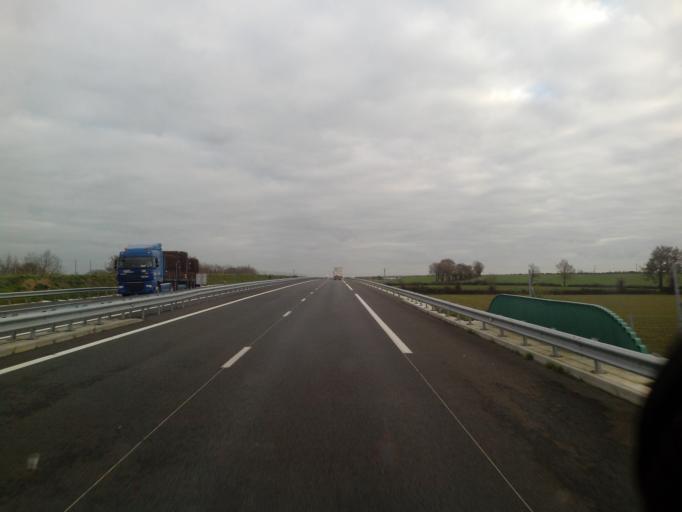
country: FR
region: Poitou-Charentes
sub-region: Departement des Deux-Sevres
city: Nueil-les-Aubiers
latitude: 46.8744
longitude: -0.5835
